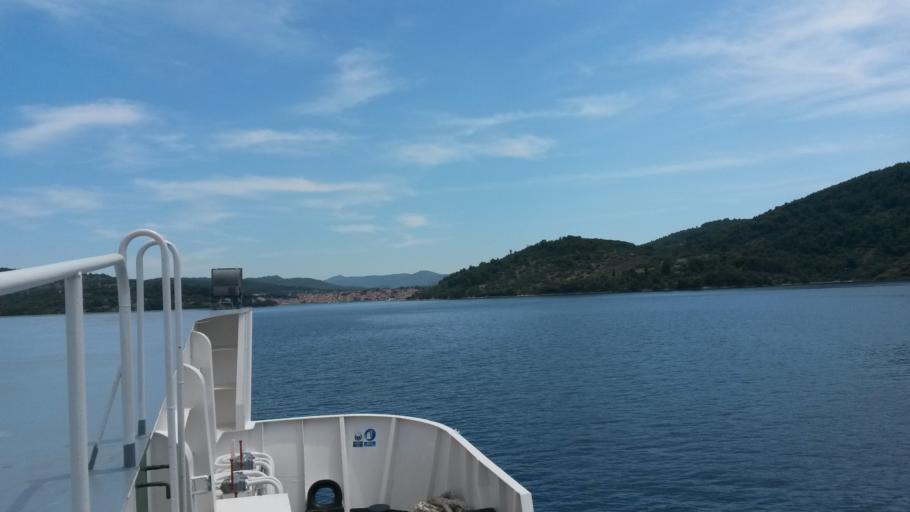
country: HR
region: Dubrovacko-Neretvanska
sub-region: Grad Dubrovnik
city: Vela Luka
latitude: 42.9635
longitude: 16.6867
